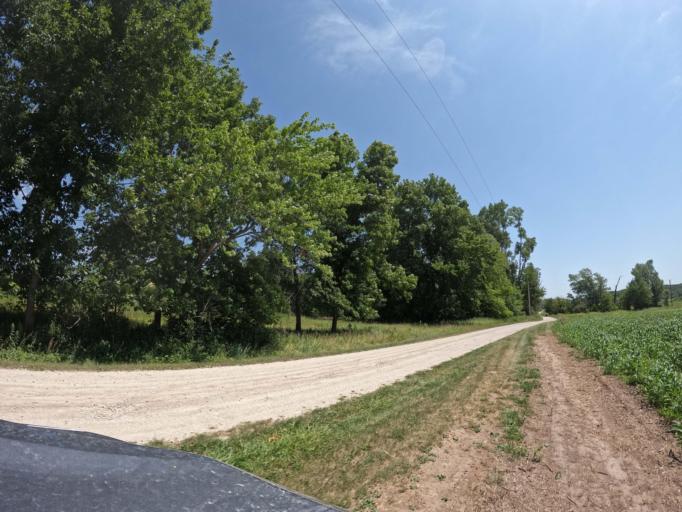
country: US
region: Iowa
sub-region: Henry County
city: Mount Pleasant
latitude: 40.9011
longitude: -91.5616
